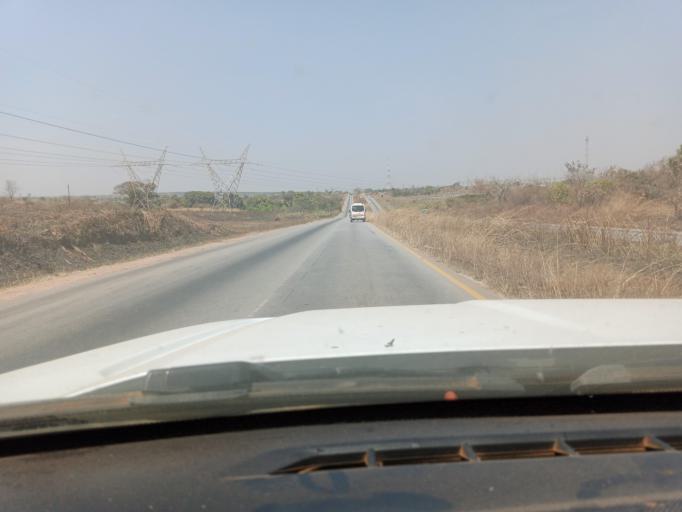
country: ZM
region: Copperbelt
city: Luanshya
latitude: -12.9679
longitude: 28.3974
